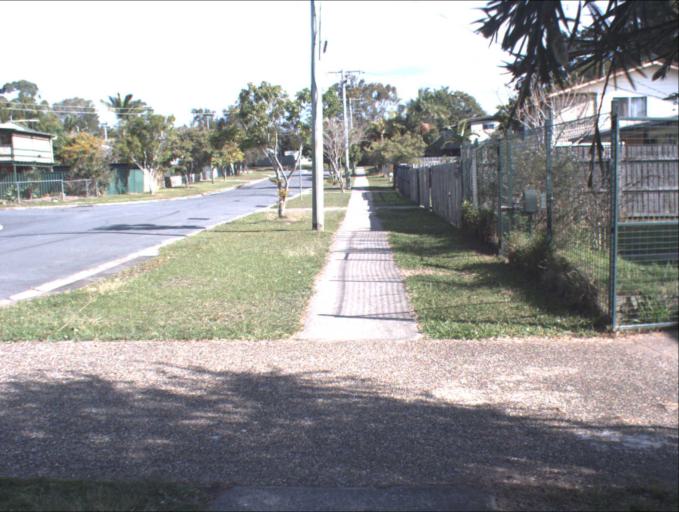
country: AU
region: Queensland
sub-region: Logan
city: Waterford West
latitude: -27.6825
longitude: 153.1167
